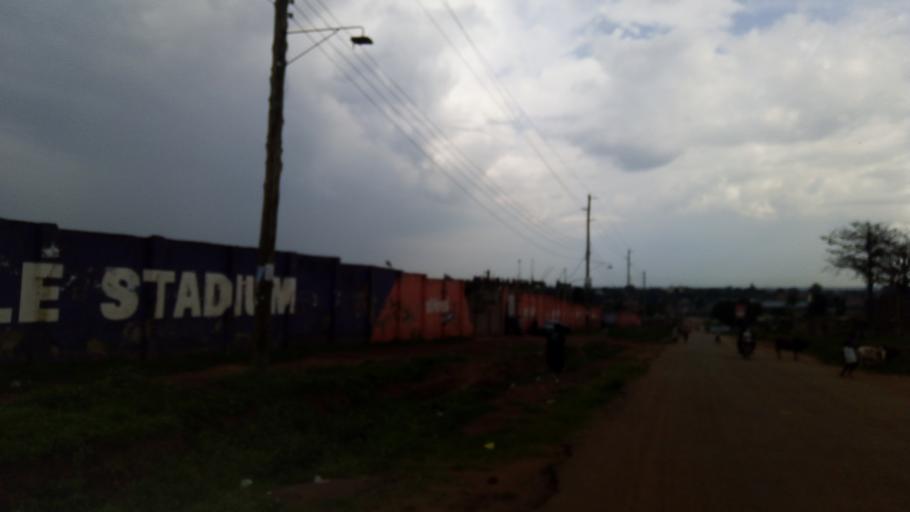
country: UG
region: Eastern Region
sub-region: Mbale District
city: Mbale
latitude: 1.0790
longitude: 34.1651
